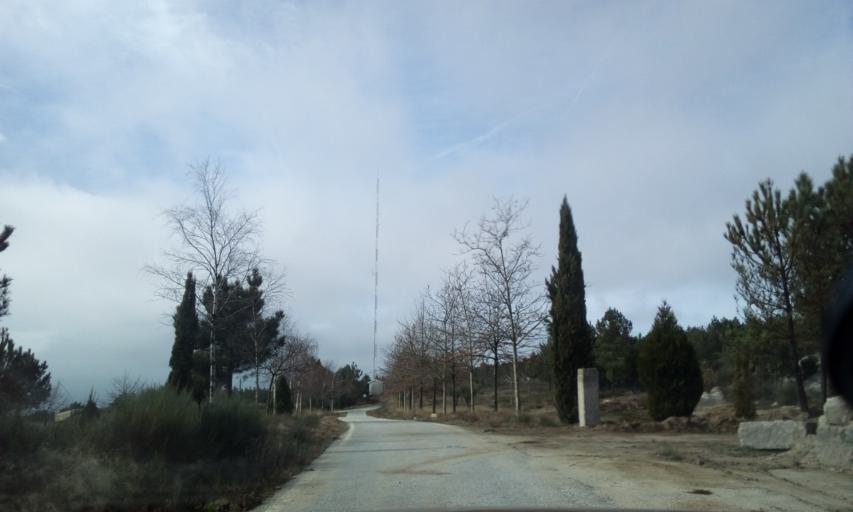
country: PT
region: Guarda
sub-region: Fornos de Algodres
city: Fornos de Algodres
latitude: 40.6376
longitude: -7.5377
